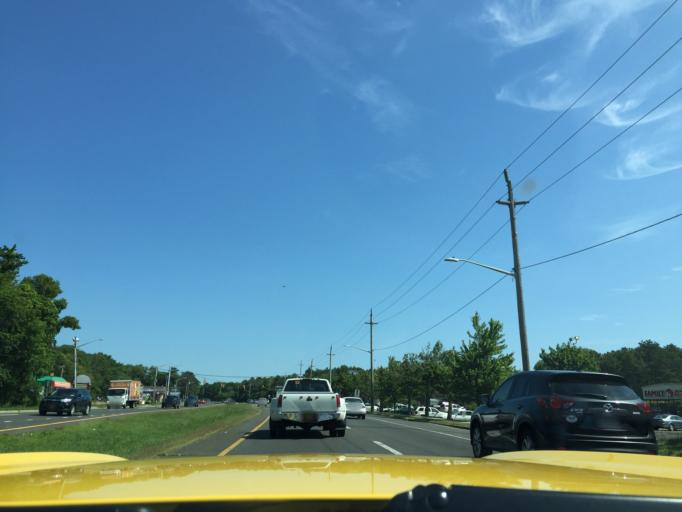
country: US
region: New York
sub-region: Suffolk County
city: Shirley
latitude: 40.7845
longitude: -72.8639
